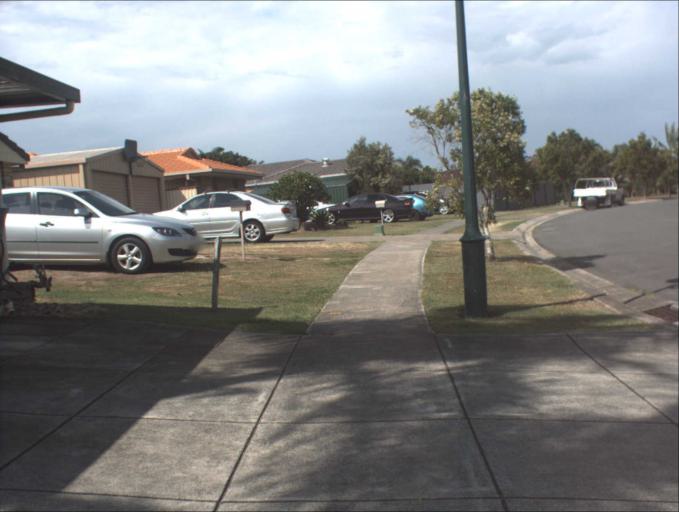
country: AU
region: Queensland
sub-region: Logan
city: Slacks Creek
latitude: -27.6807
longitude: 153.1723
